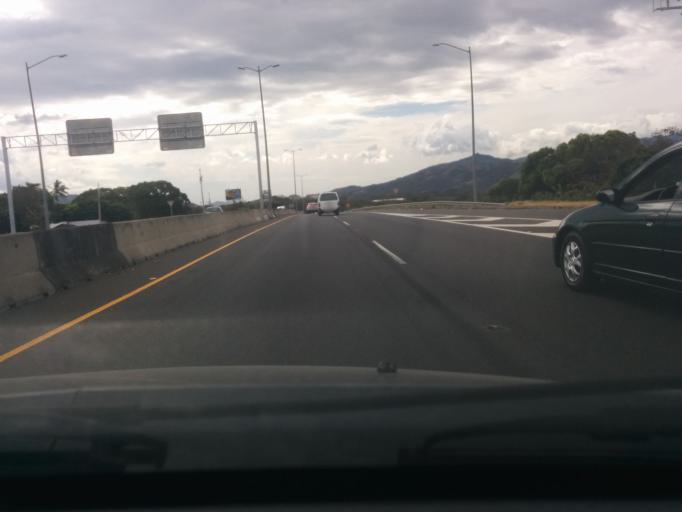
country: CR
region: Alajuela
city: Atenas
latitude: 9.9651
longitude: -84.3135
